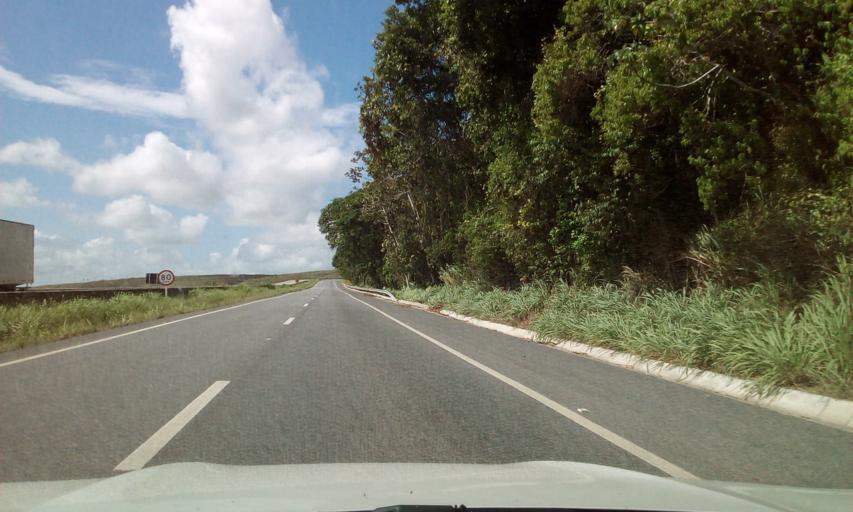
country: BR
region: Alagoas
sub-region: Rio Largo
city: Rio Largo
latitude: -9.4650
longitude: -35.8793
